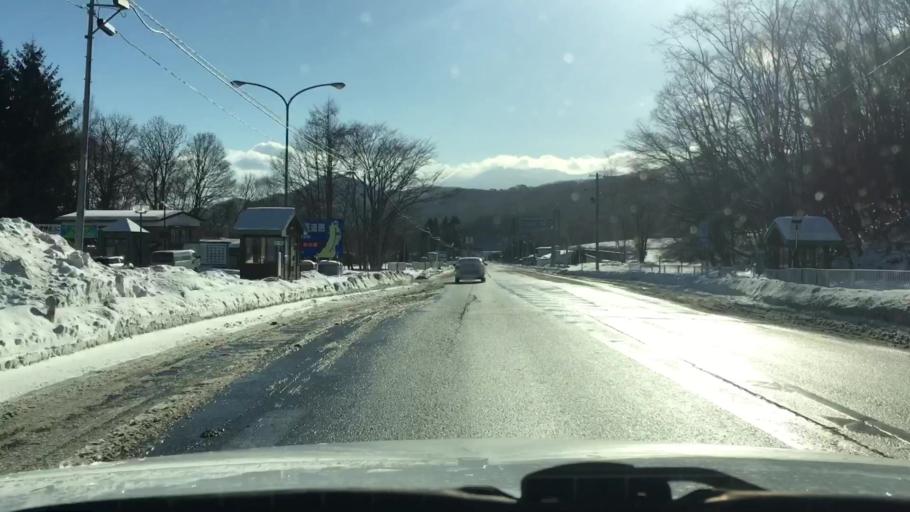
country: JP
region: Iwate
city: Morioka-shi
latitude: 39.6511
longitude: 141.3532
